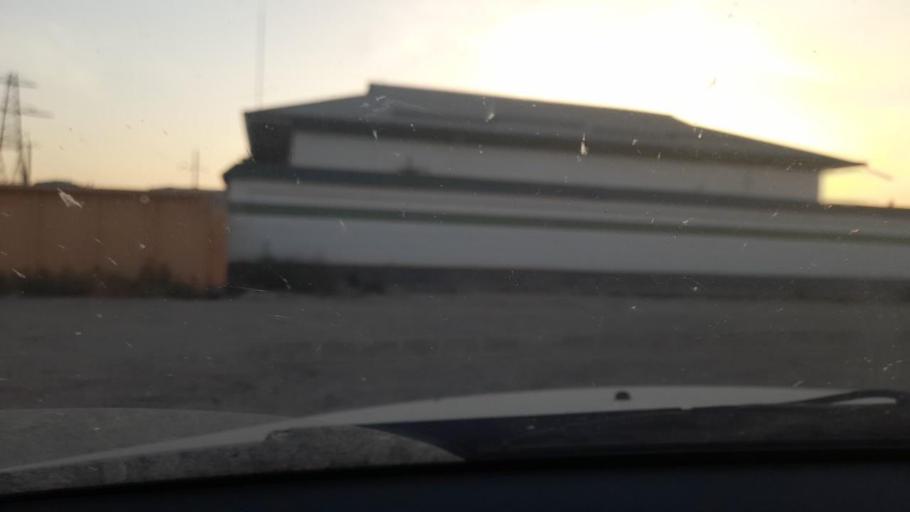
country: UZ
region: Sirdaryo
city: Guliston
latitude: 40.5105
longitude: 68.7624
